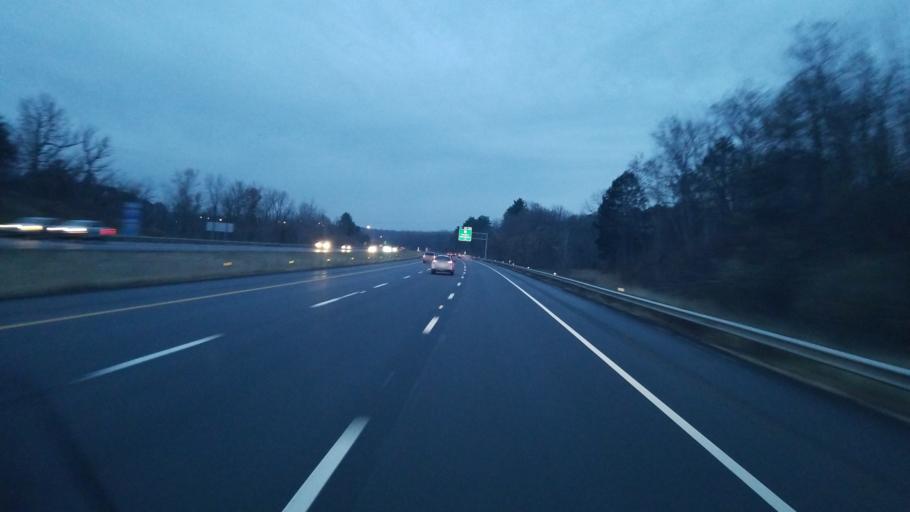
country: US
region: Ohio
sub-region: Richland County
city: Lincoln Heights
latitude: 40.7974
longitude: -82.3969
